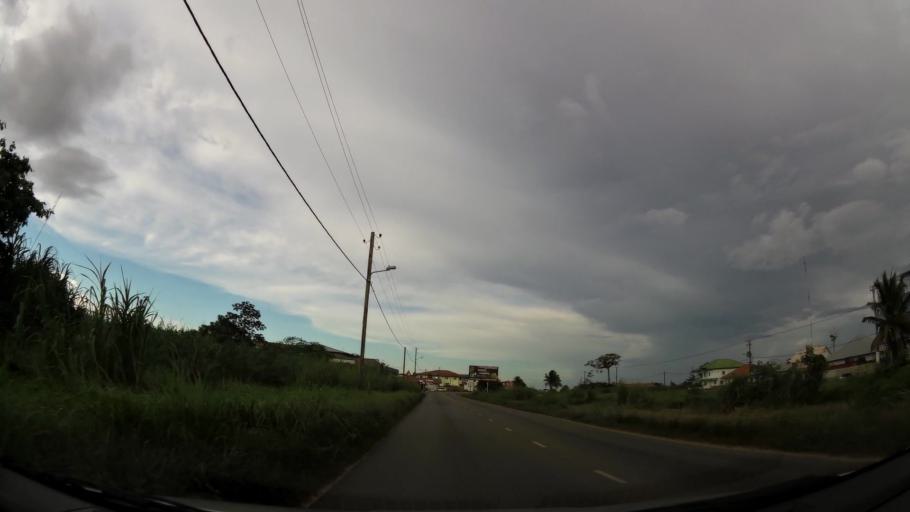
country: SR
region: Paramaribo
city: Paramaribo
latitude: 5.8566
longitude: -55.1629
